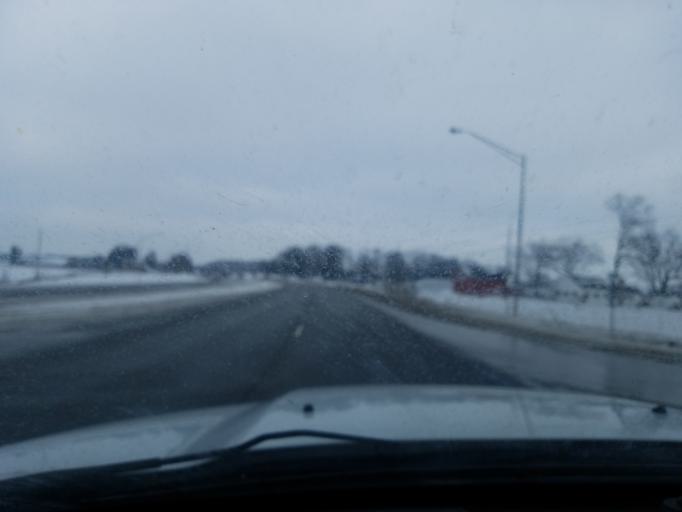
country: US
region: Indiana
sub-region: Marshall County
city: Plymouth
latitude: 41.2878
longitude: -86.2706
